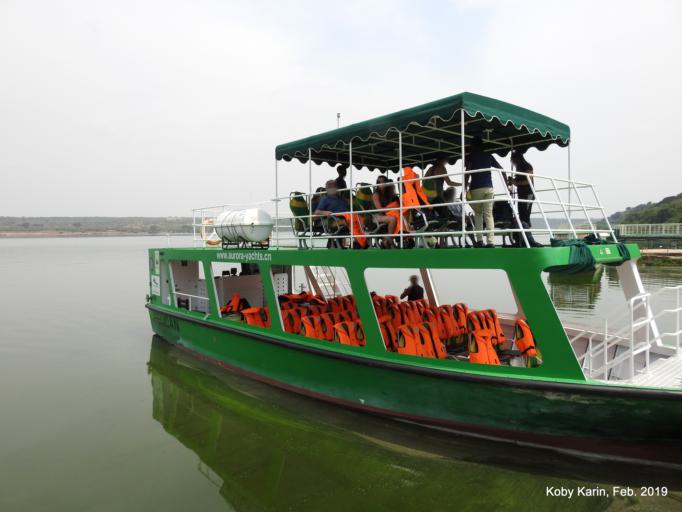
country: UG
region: Western Region
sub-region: Rubirizi District
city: Rubirizi
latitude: -0.1867
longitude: 29.9001
